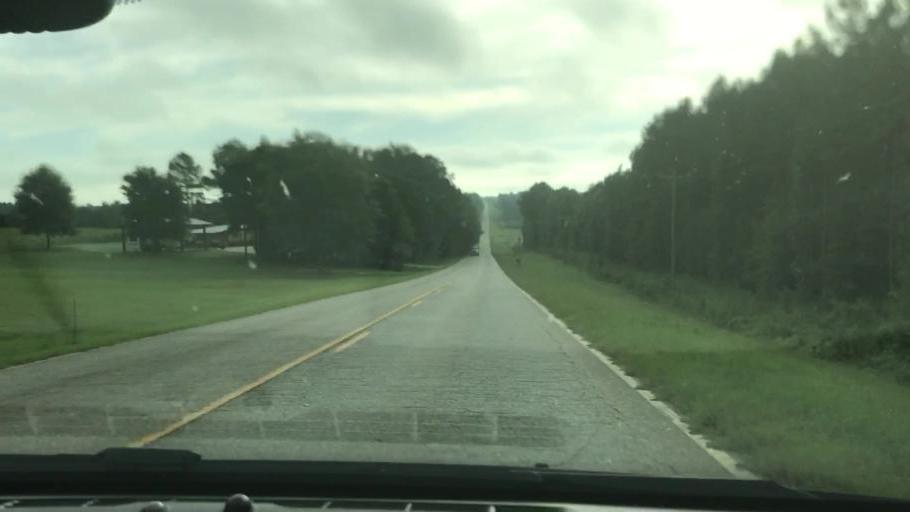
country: US
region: Georgia
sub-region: Quitman County
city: Georgetown
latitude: 31.8926
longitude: -85.0781
